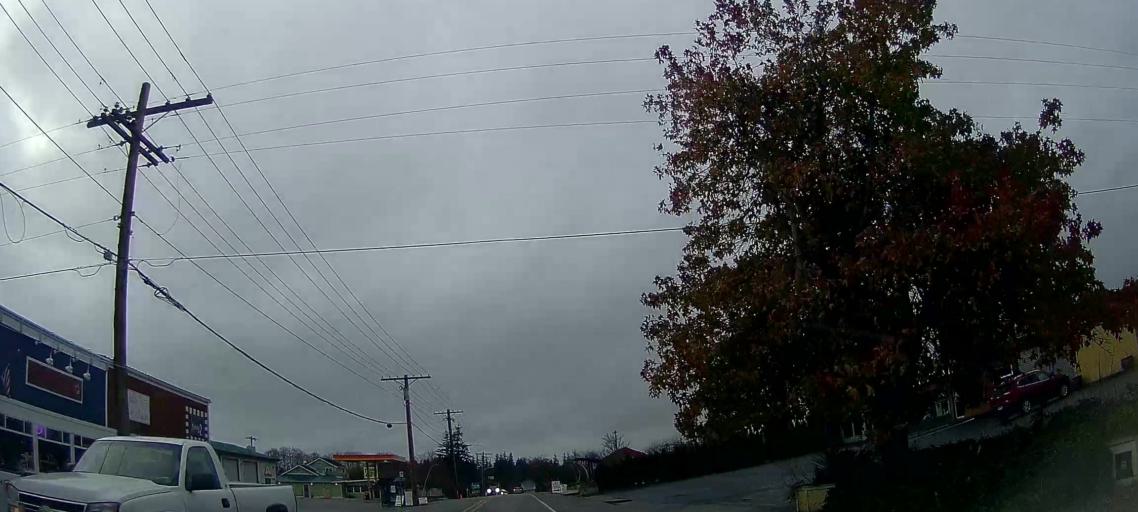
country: US
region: Washington
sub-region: Island County
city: Freeland
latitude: 48.0096
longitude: -122.5250
